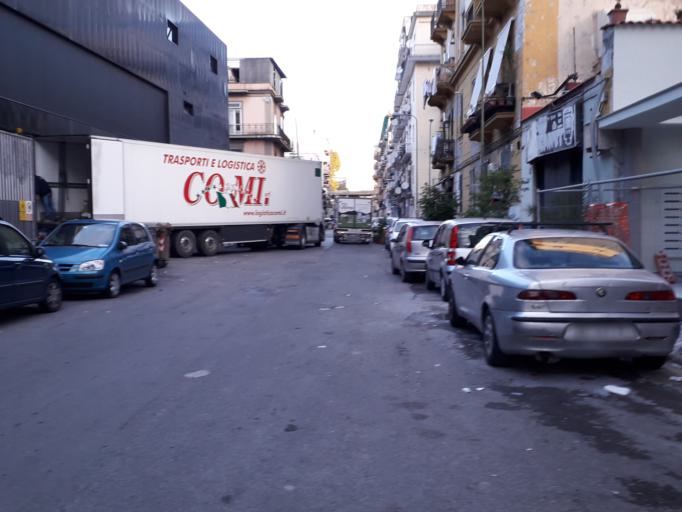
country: IT
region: Campania
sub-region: Provincia di Napoli
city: Napoli
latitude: 40.8625
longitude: 14.2711
